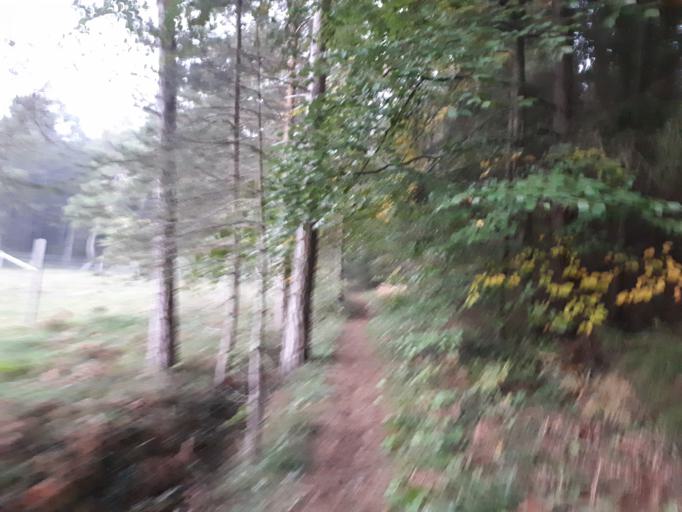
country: SE
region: Gotland
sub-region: Gotland
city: Visby
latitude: 57.6866
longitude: 18.3501
